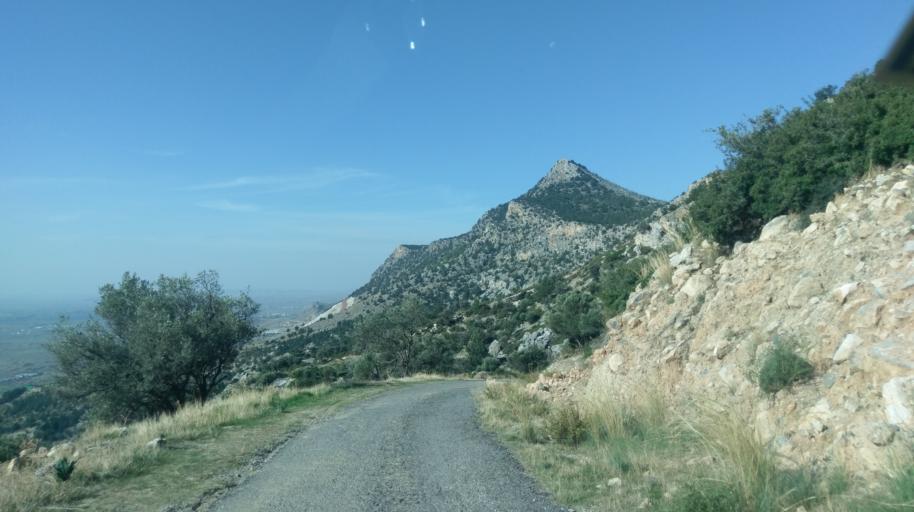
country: CY
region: Keryneia
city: Kyrenia
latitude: 35.2849
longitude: 33.3978
